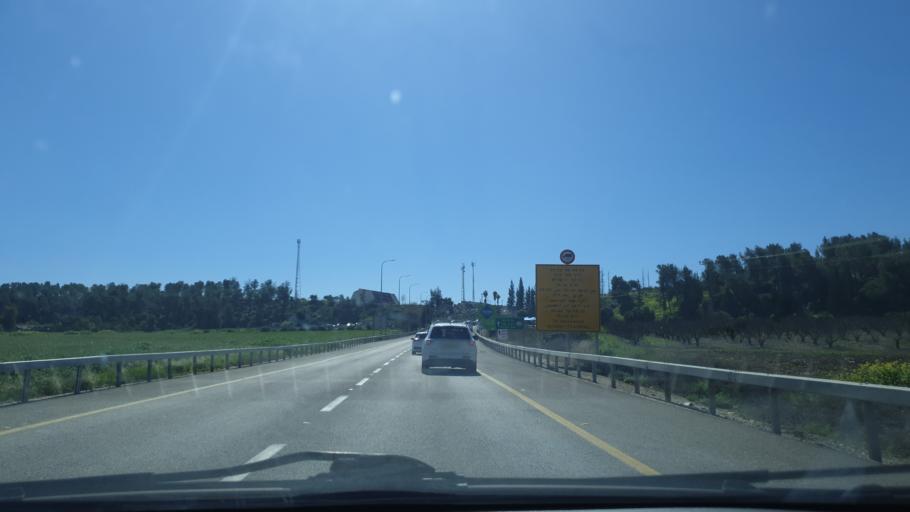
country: IL
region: Jerusalem
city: Bet Shemesh
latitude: 31.6901
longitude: 34.9447
